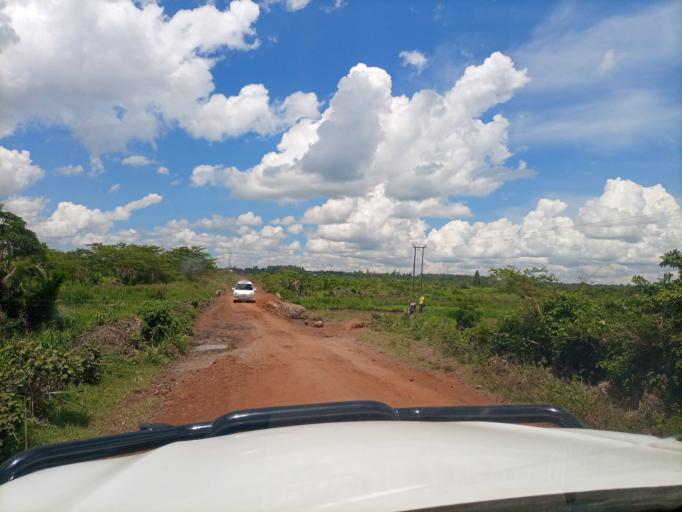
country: UG
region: Eastern Region
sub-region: Busia District
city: Busia
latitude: 0.6237
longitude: 33.9891
